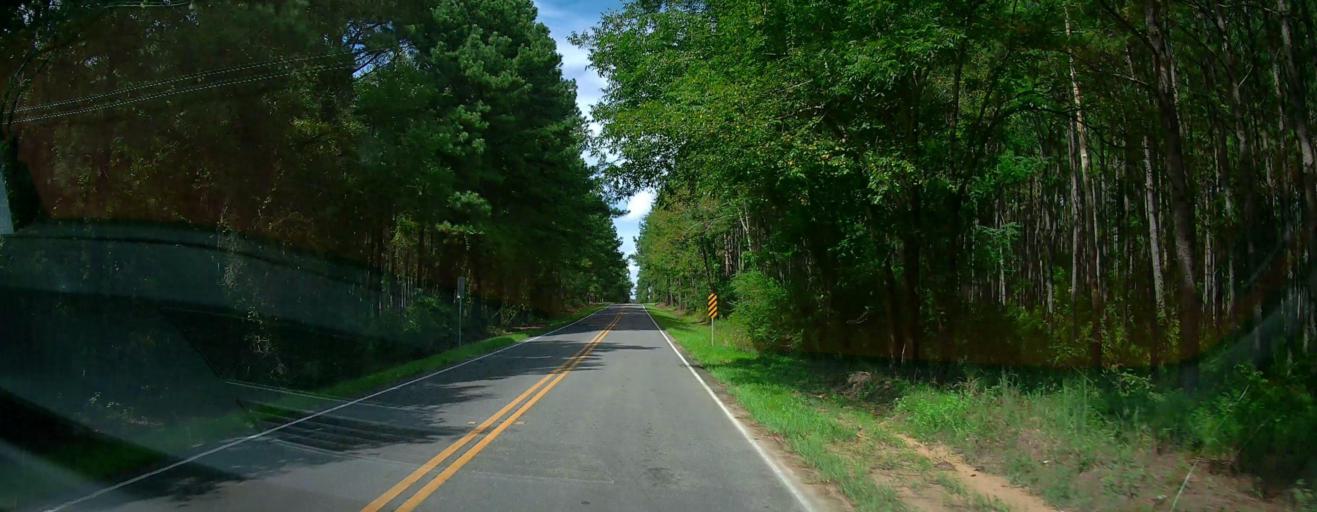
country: US
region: Georgia
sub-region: Taylor County
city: Butler
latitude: 32.5021
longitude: -84.2022
